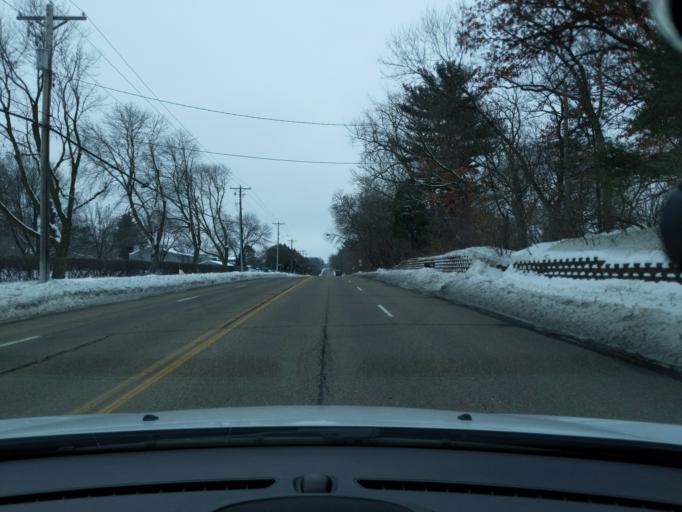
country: US
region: Minnesota
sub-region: Ramsey County
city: Roseville
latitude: 45.0207
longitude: -93.1241
